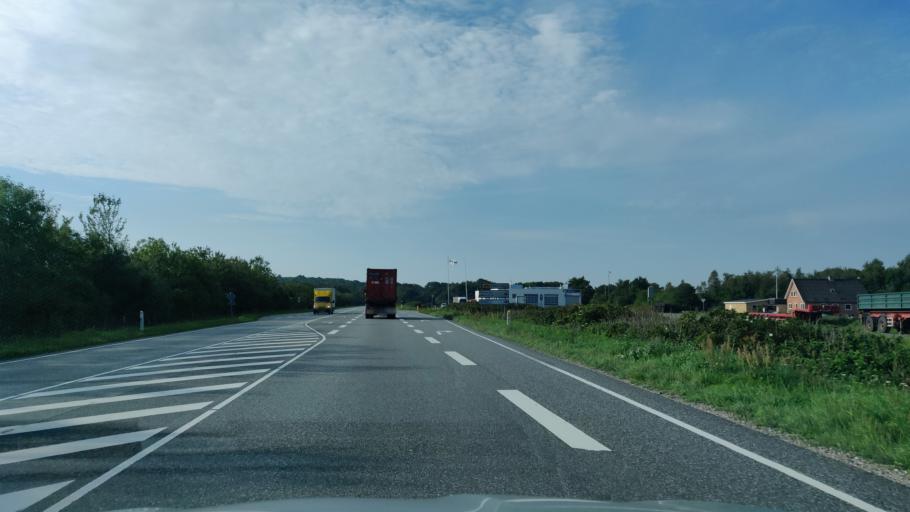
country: DK
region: North Denmark
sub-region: Vesthimmerland Kommune
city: Alestrup
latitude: 56.7425
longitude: 9.5373
